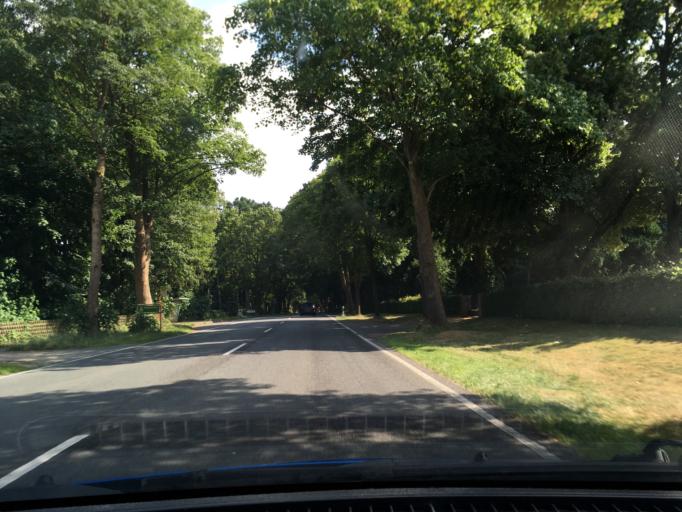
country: DE
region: Lower Saxony
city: Welle
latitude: 53.2327
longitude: 9.8043
